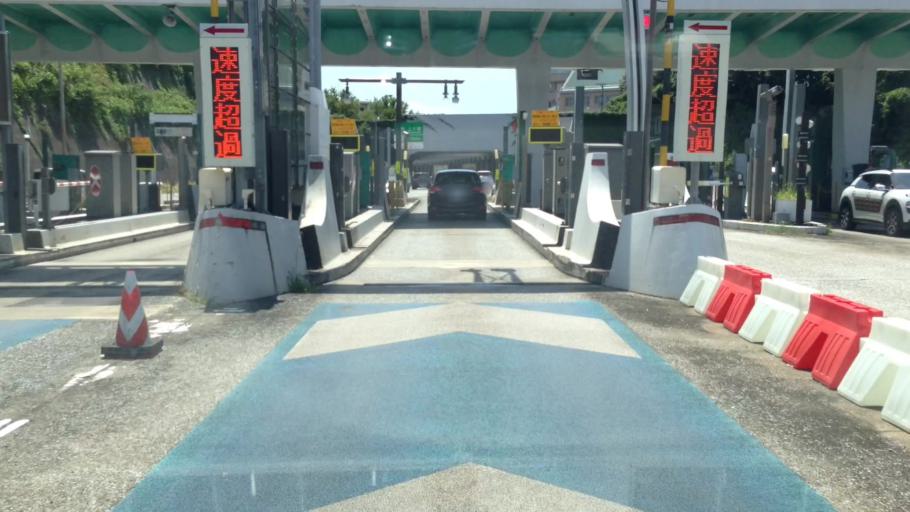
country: JP
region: Kanagawa
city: Yokohama
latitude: 35.4237
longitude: 139.5812
